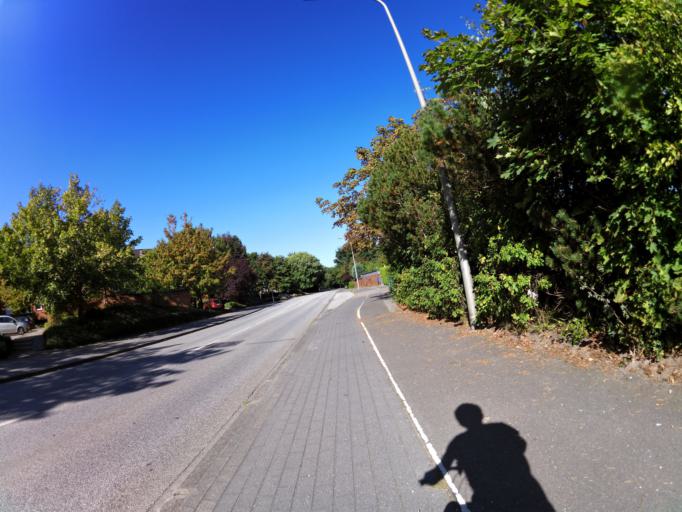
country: DE
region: Schleswig-Holstein
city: Eckernforde
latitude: 54.4579
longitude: 9.8294
